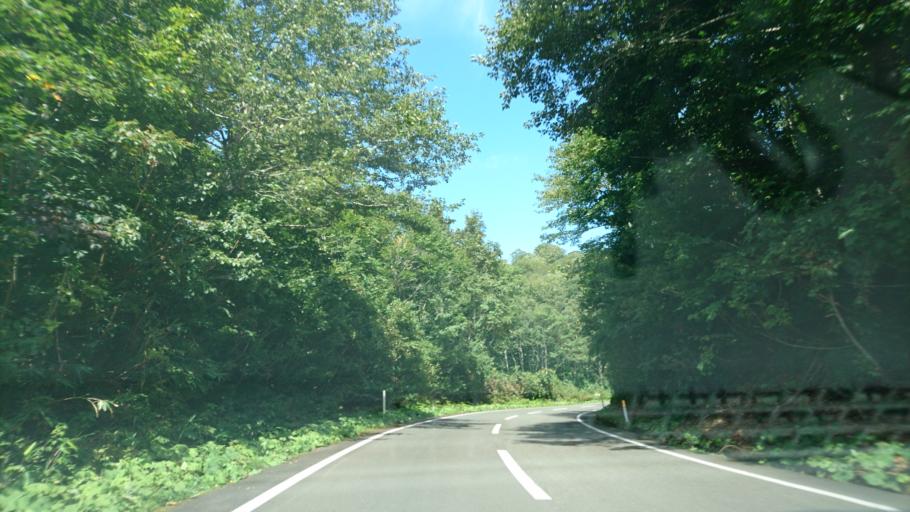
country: JP
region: Akita
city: Yuzawa
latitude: 38.9543
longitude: 140.7156
